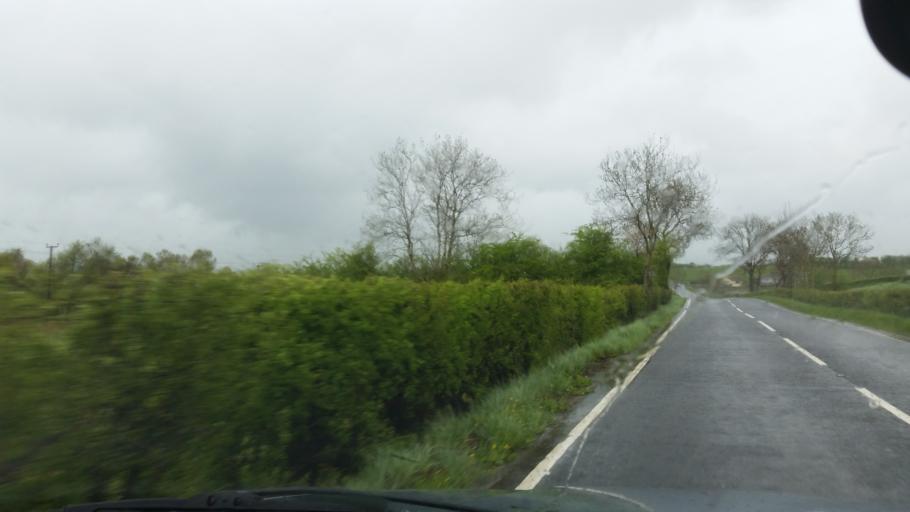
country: GB
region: Northern Ireland
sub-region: Omagh District
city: Omagh
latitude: 54.5499
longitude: -7.2850
